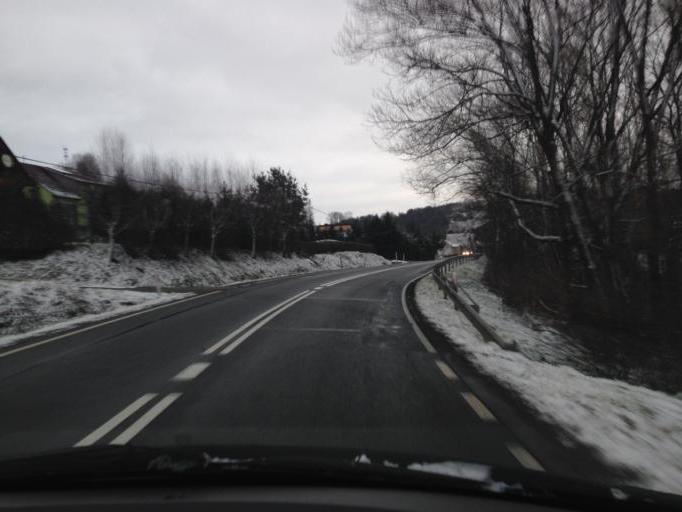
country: PL
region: Lesser Poland Voivodeship
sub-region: Powiat tarnowski
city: Rzepiennik Strzyzewski
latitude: 49.8089
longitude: 21.0281
